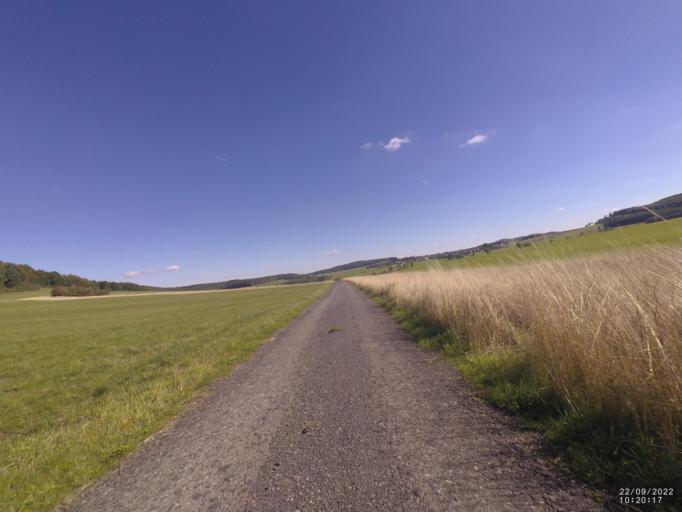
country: DE
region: Rheinland-Pfalz
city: Walsdorf
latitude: 50.2837
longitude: 6.7309
